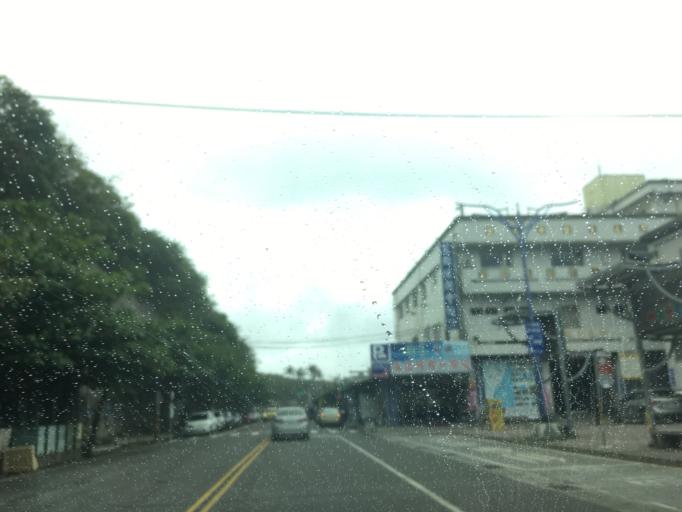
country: TW
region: Taiwan
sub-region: Taitung
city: Taitung
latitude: 22.7919
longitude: 121.1927
